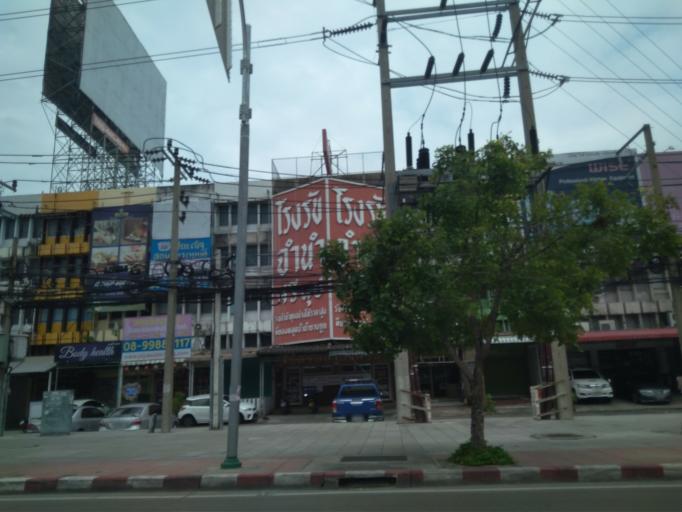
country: TH
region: Bangkok
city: Suan Luang
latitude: 13.7135
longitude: 100.6437
